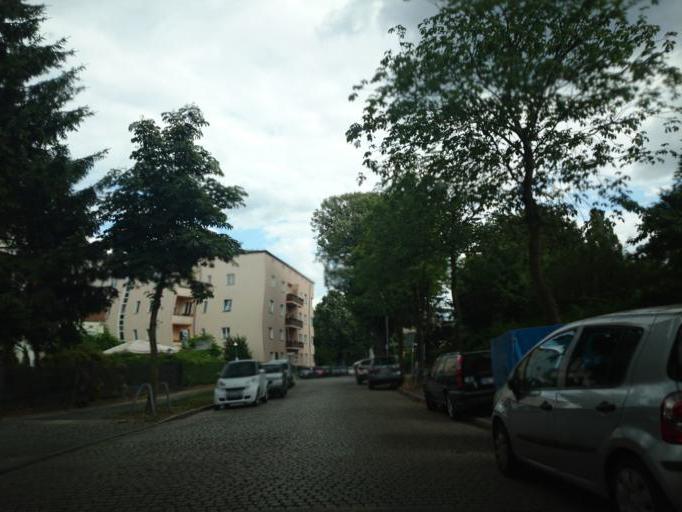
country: DE
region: Berlin
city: Lichterfelde
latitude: 52.4414
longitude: 13.3140
